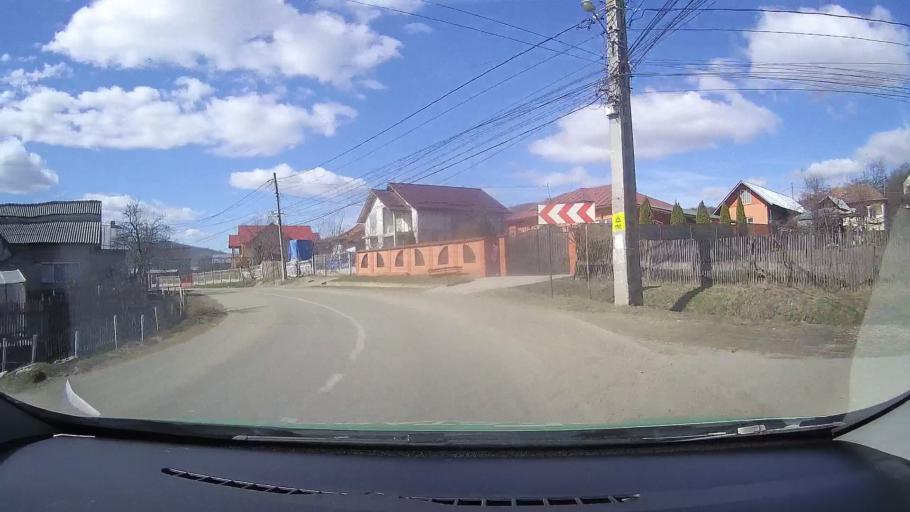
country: RO
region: Dambovita
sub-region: Comuna Glodeni
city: Glodeni
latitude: 45.0210
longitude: 25.4504
